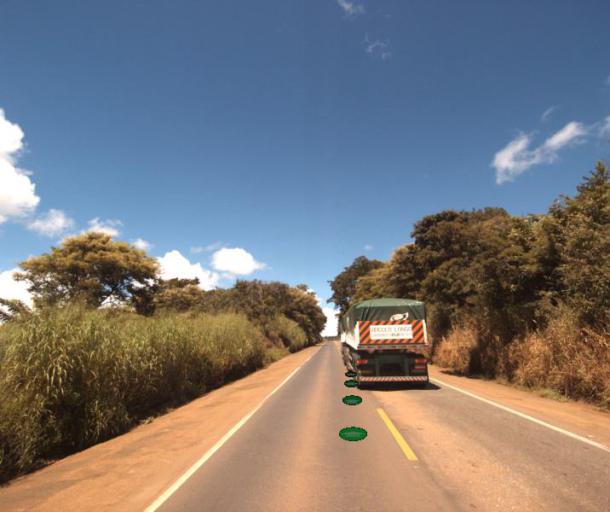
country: BR
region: Goias
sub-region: Anapolis
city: Anapolis
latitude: -16.1657
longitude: -49.0433
